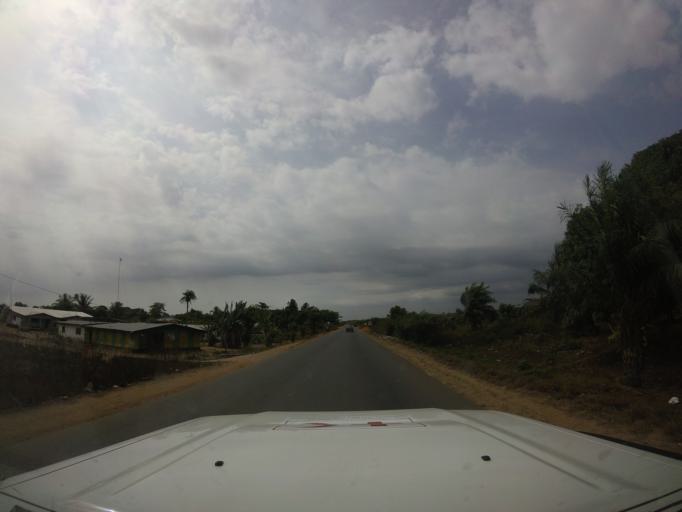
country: LR
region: Montserrado
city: Monrovia
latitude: 6.4586
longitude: -10.8052
